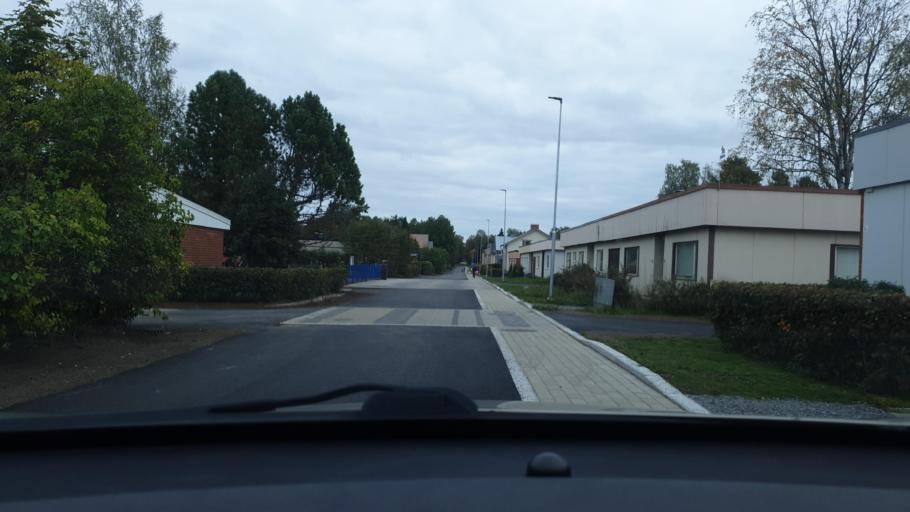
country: FI
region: Ostrobothnia
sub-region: Vaasa
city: Korsholm
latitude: 63.0963
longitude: 21.6697
